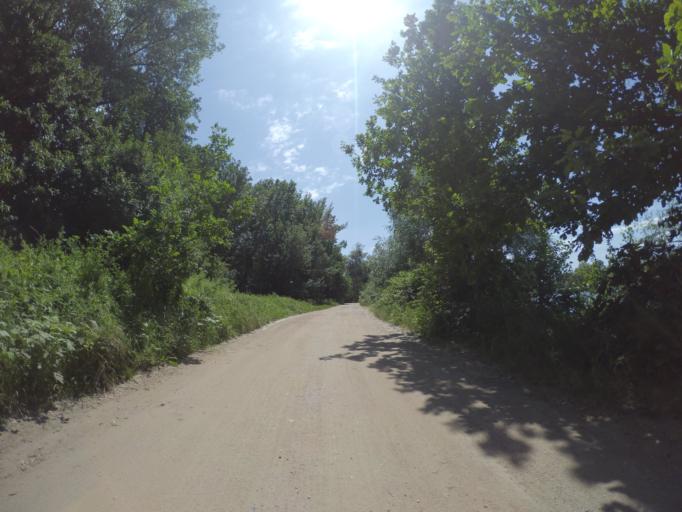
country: CZ
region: Central Bohemia
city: Milovice
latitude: 50.1765
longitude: 14.9012
